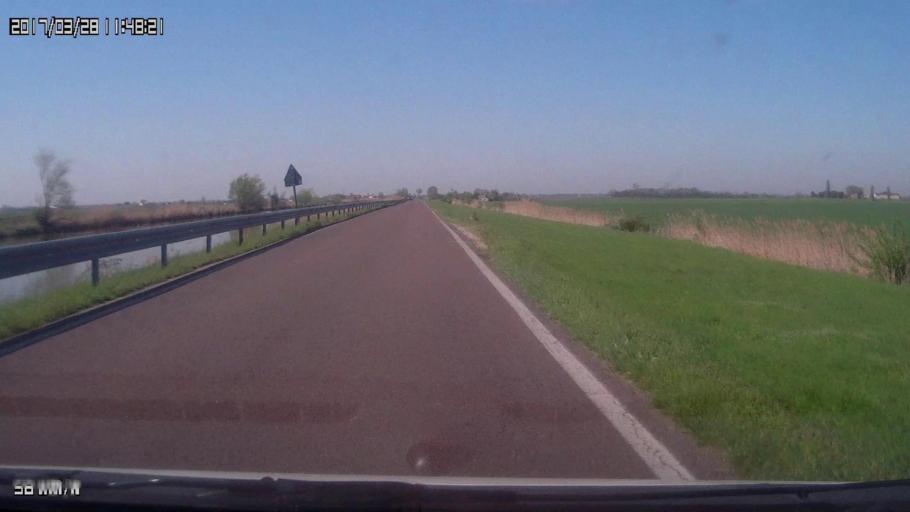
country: IT
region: Veneto
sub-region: Provincia di Venezia
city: Sant'Anna
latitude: 45.1620
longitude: 12.2236
